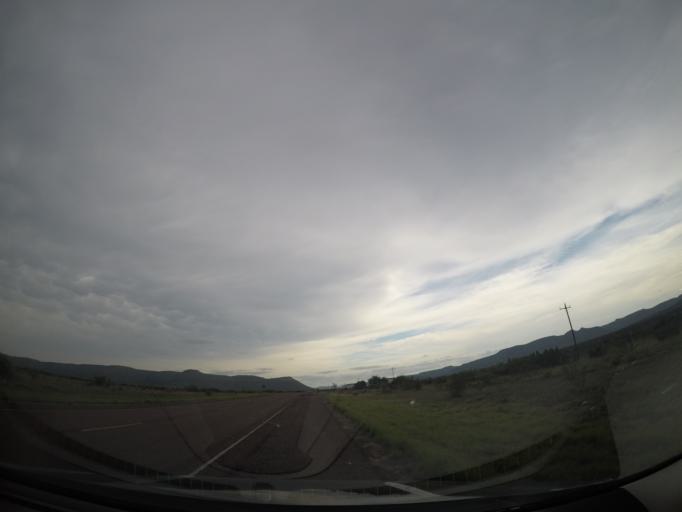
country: US
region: Texas
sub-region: Terrell County
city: Sanderson
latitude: 30.2014
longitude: -102.9143
